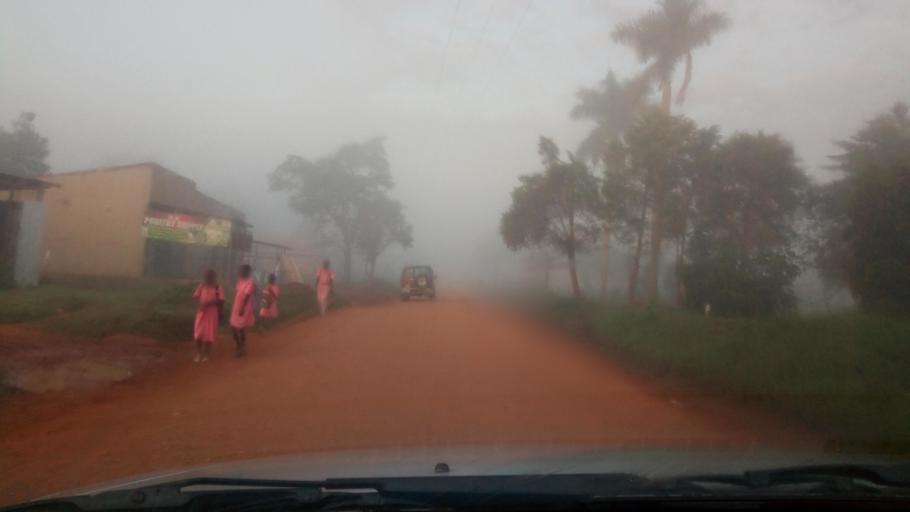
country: UG
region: Central Region
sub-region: Wakiso District
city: Bweyogerere
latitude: 0.4370
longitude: 32.6551
